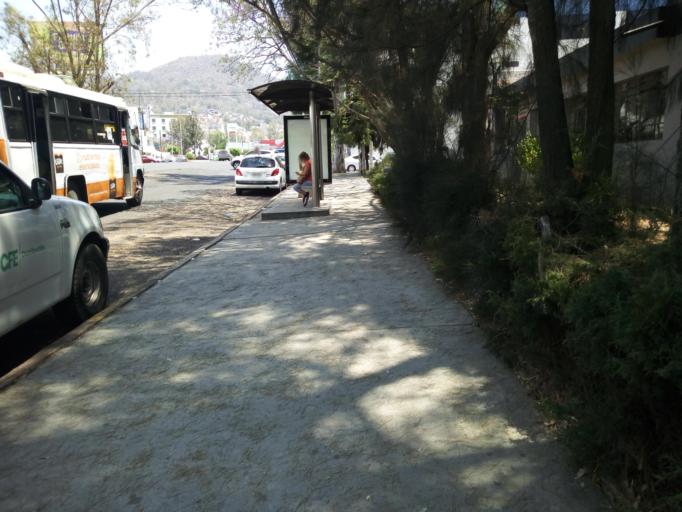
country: MX
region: Michoacan
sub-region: Morelia
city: Puerto de Buenavista (Lazaro Cardenas)
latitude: 19.6947
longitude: -101.1514
